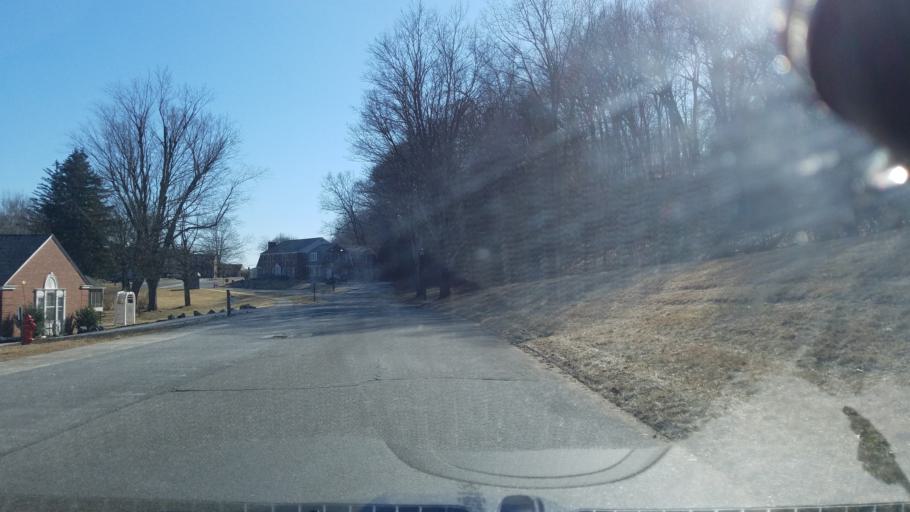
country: US
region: Connecticut
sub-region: New Haven County
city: Heritage Village
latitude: 41.4908
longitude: -73.2640
